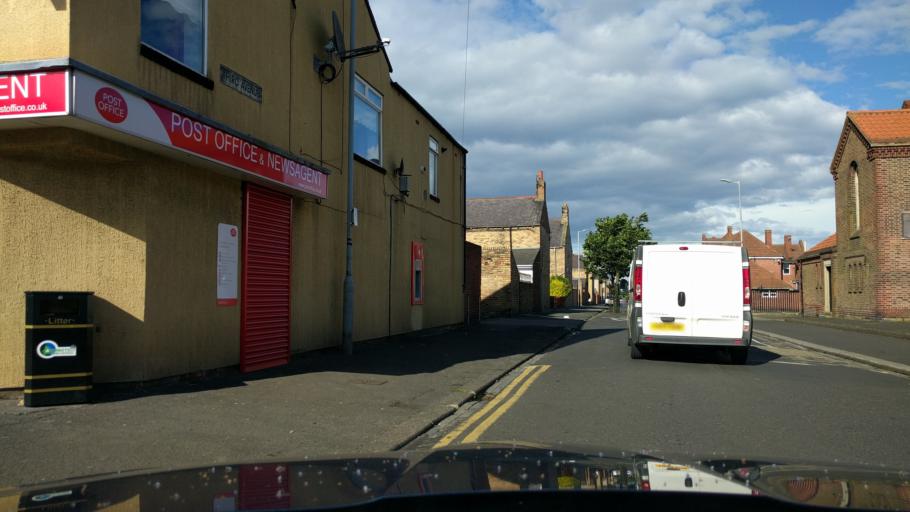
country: GB
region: England
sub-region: Northumberland
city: Ashington
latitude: 55.1799
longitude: -1.5612
